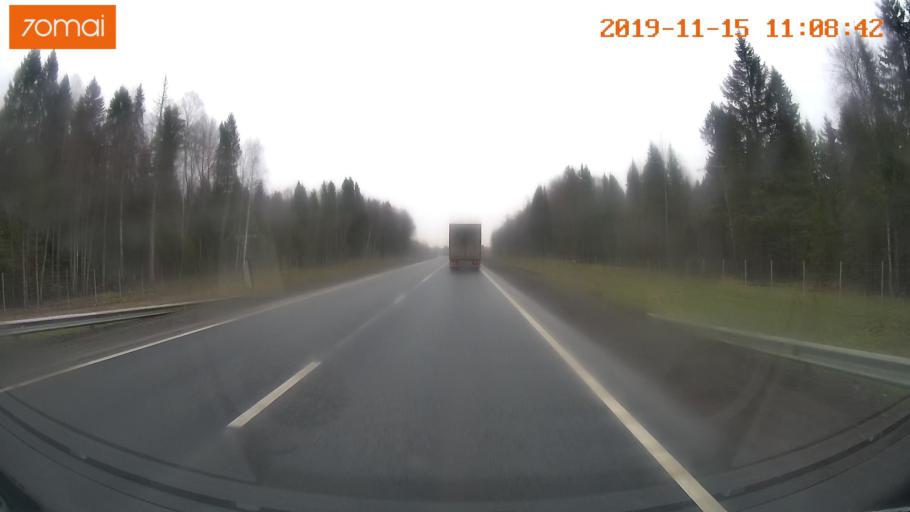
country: RU
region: Vologda
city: Chebsara
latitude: 59.1201
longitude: 39.0807
